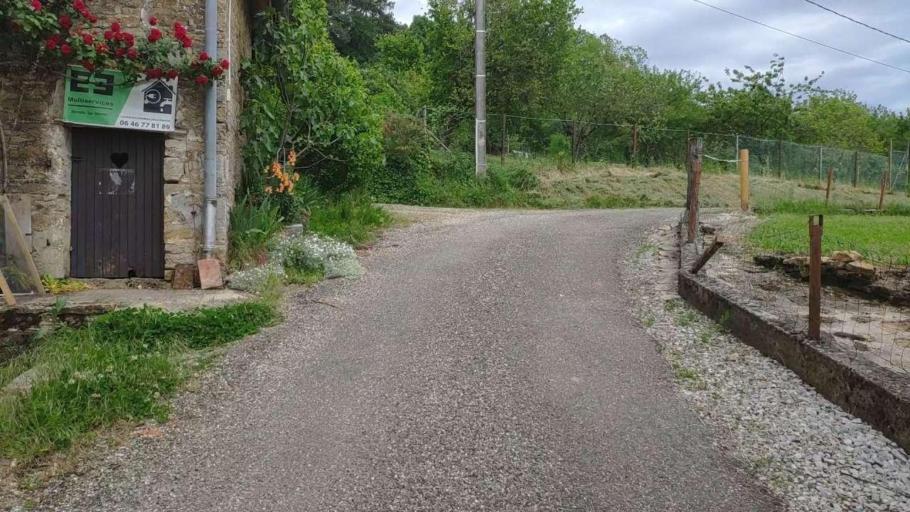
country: FR
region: Franche-Comte
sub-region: Departement du Jura
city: Bletterans
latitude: 46.7848
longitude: 5.5652
